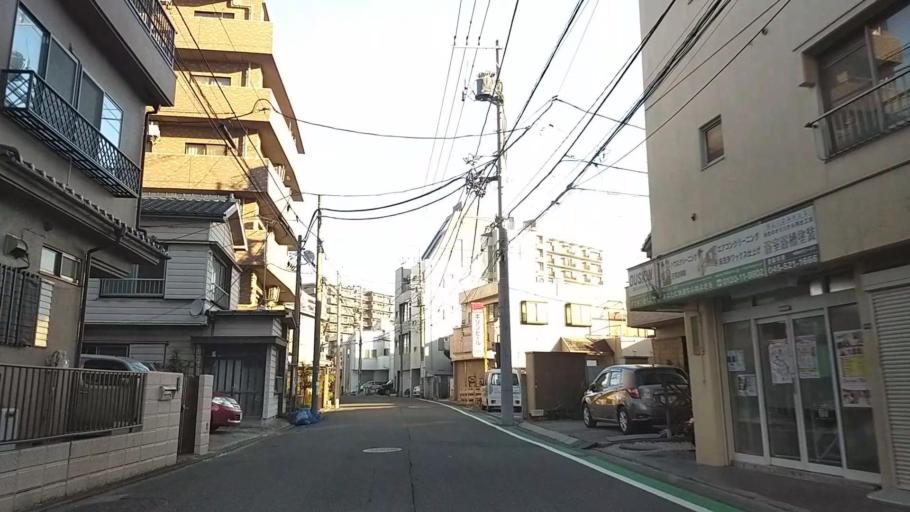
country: JP
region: Kanagawa
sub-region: Kawasaki-shi
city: Kawasaki
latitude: 35.5011
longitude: 139.6762
